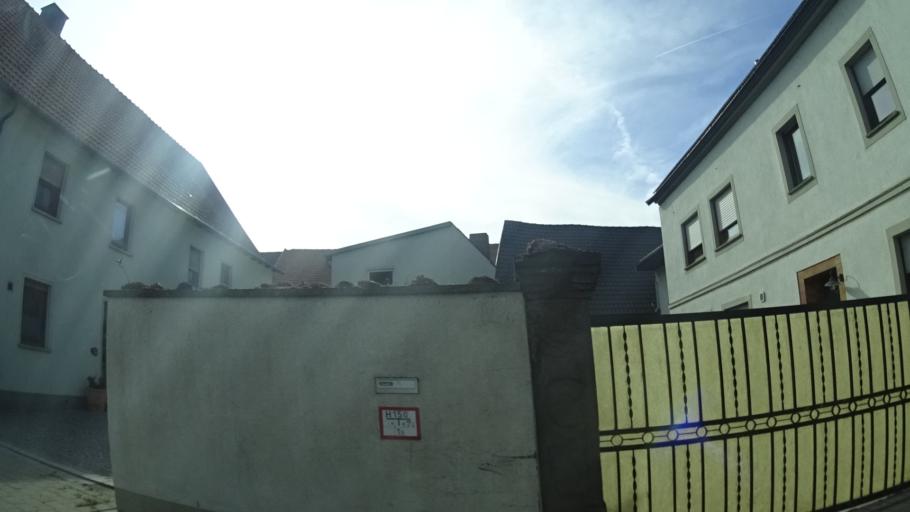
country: DE
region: Bavaria
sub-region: Regierungsbezirk Unterfranken
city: Kolitzheim
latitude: 49.9192
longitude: 10.2362
